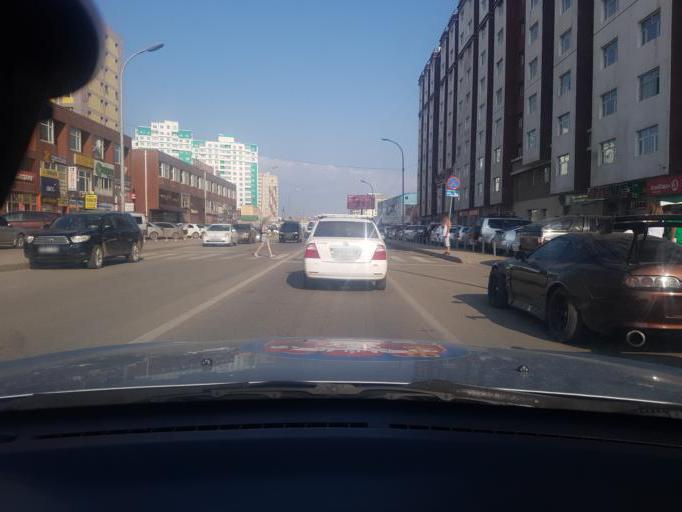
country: MN
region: Ulaanbaatar
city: Ulaanbaatar
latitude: 47.9238
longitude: 106.9780
